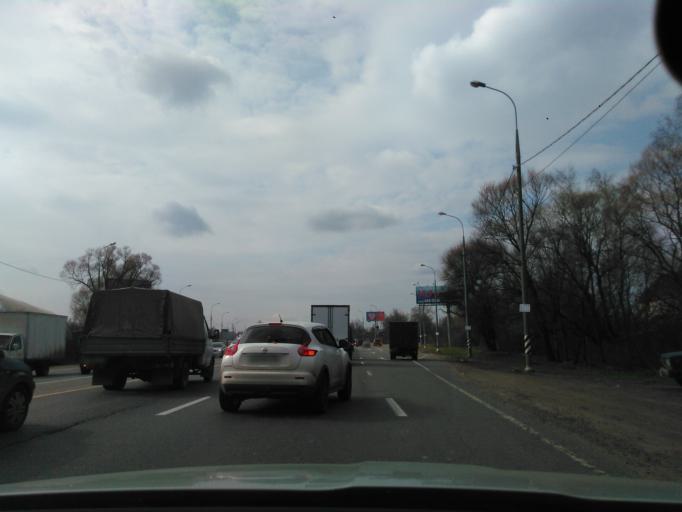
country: RU
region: Moskovskaya
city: Sheremet'yevskiy
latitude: 55.9805
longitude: 37.5258
